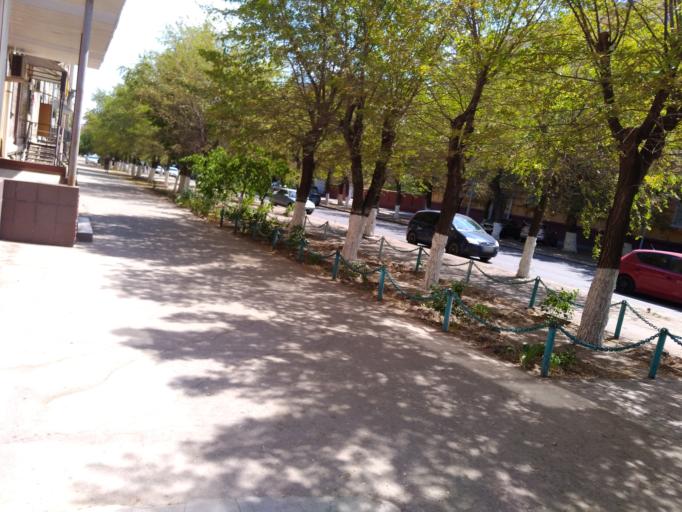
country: RU
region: Volgograd
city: Volgograd
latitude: 48.7153
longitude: 44.5221
